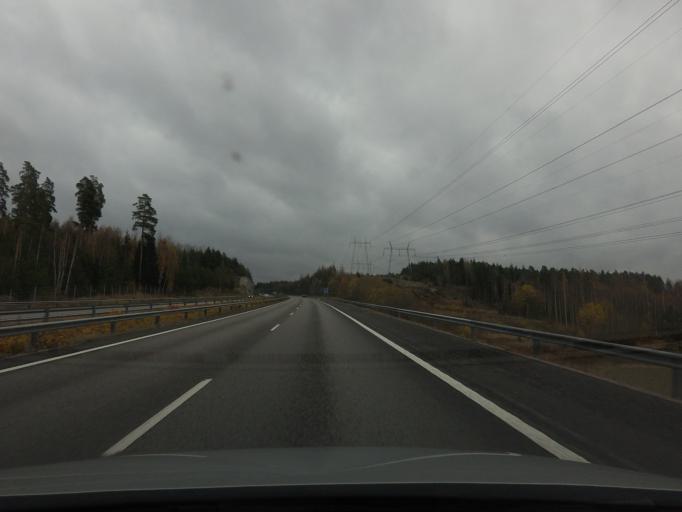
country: FI
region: Varsinais-Suomi
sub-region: Turku
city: Paimio
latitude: 60.4247
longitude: 22.6727
